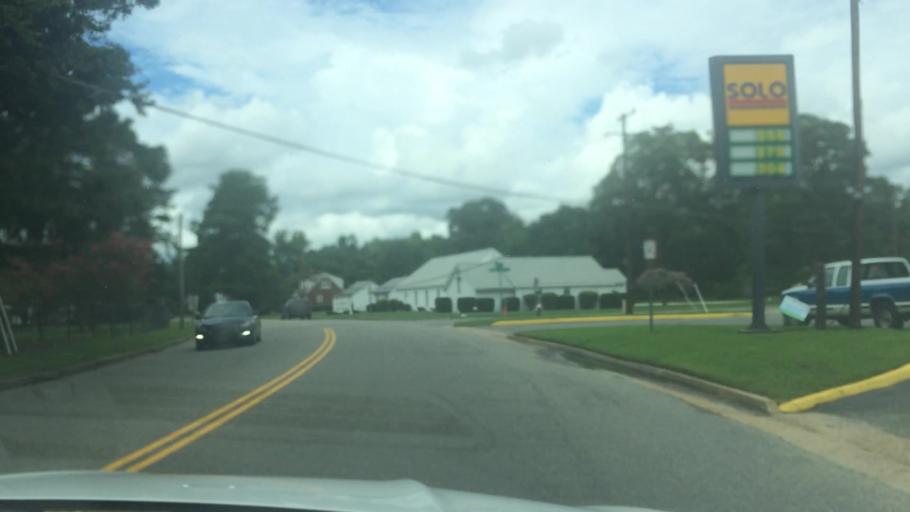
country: US
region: Virginia
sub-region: City of Williamsburg
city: Williamsburg
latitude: 37.2637
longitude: -76.6655
